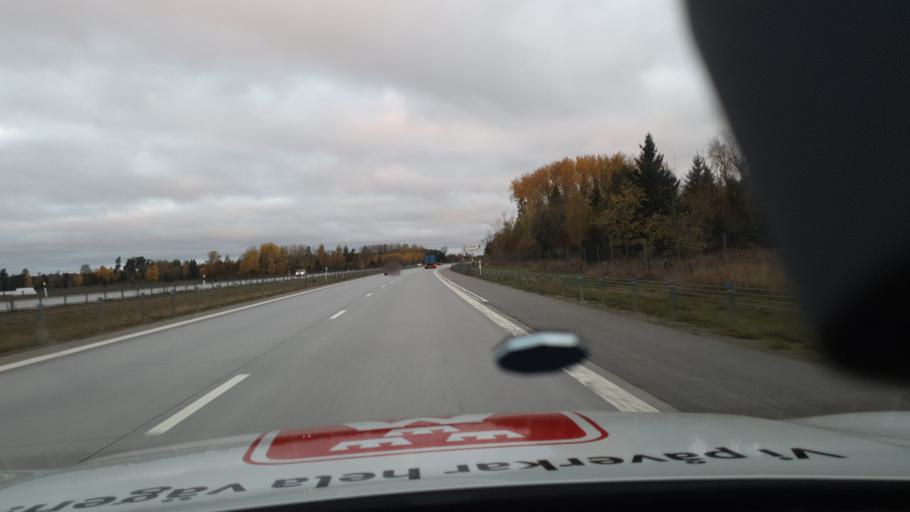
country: SE
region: Uppsala
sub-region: Uppsala Kommun
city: Storvreta
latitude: 59.9825
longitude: 17.6401
